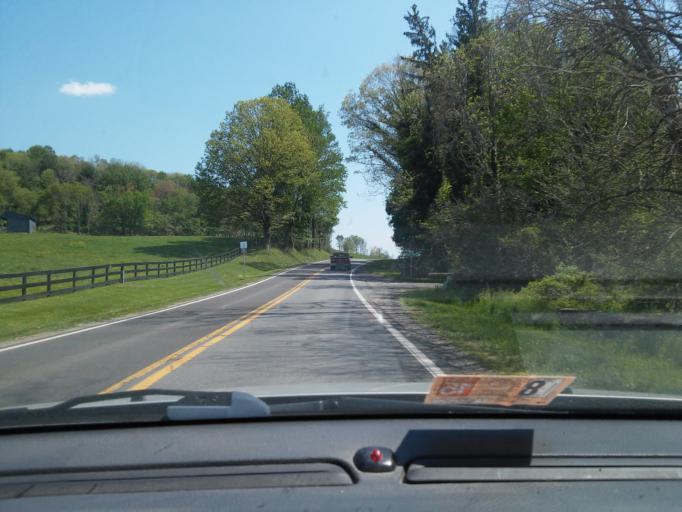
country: US
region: Virginia
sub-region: Warren County
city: Apple Mountain Lake
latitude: 38.8158
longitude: -78.1068
